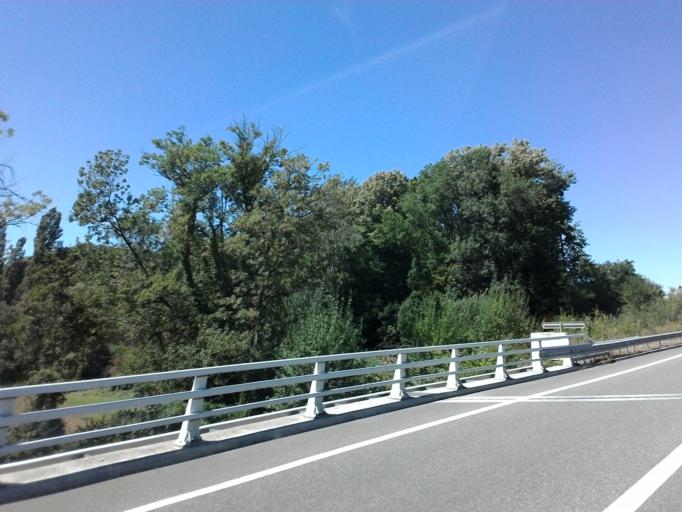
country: FR
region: Franche-Comte
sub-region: Departement du Jura
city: Montmorot
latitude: 46.6595
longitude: 5.5078
